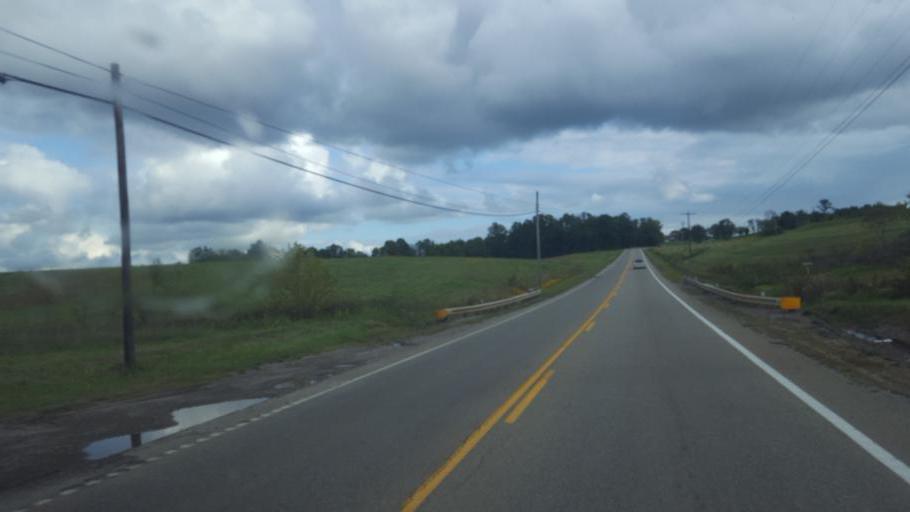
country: US
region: Ohio
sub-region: Jackson County
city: Oak Hill
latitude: 38.9302
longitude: -82.5658
